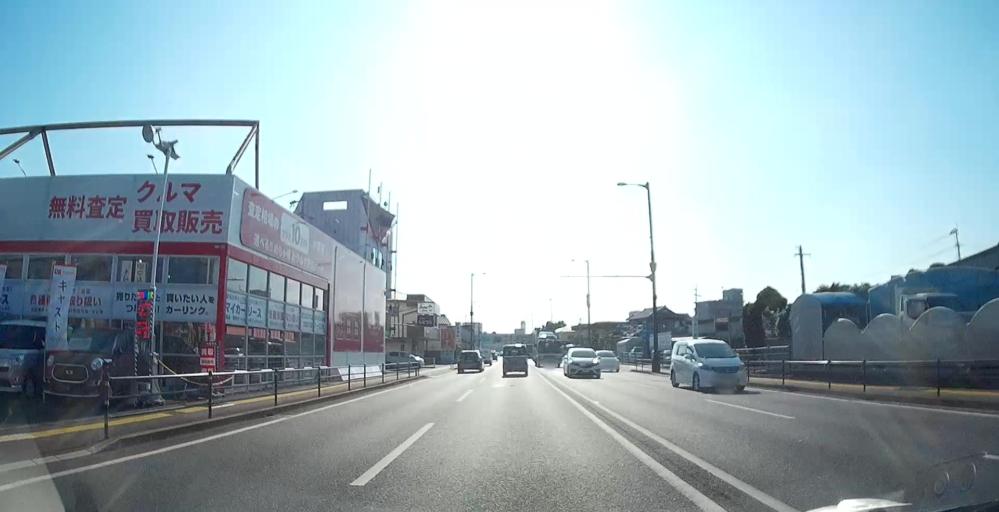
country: JP
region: Kumamoto
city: Kumamoto
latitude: 32.7646
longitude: 130.6905
